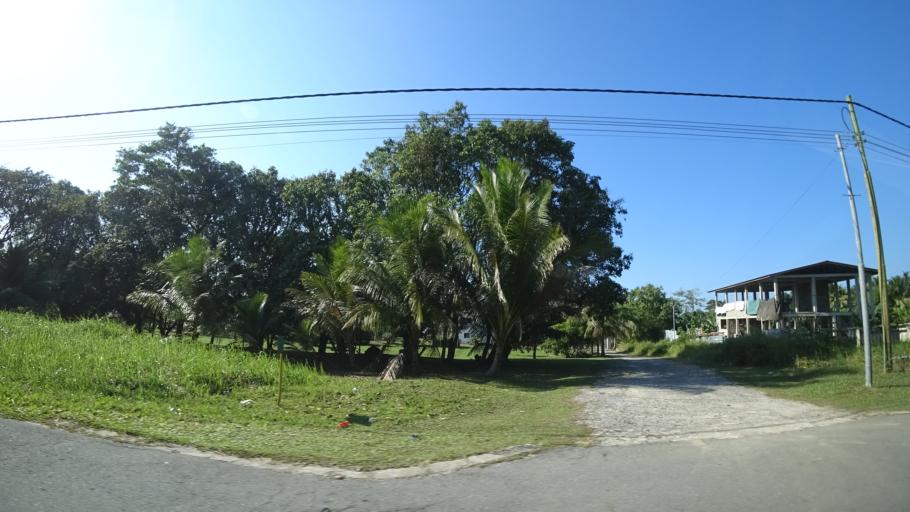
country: BN
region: Tutong
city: Tutong
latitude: 4.6868
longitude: 114.5079
